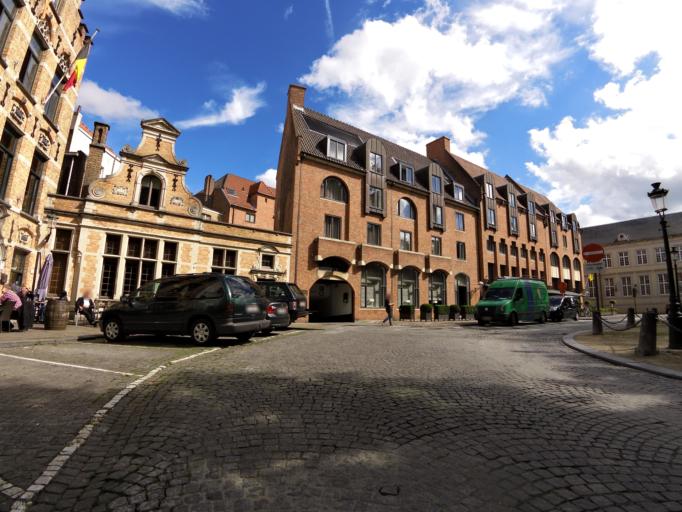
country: BE
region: Flanders
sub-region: Provincie West-Vlaanderen
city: Brugge
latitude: 51.2093
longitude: 3.2263
